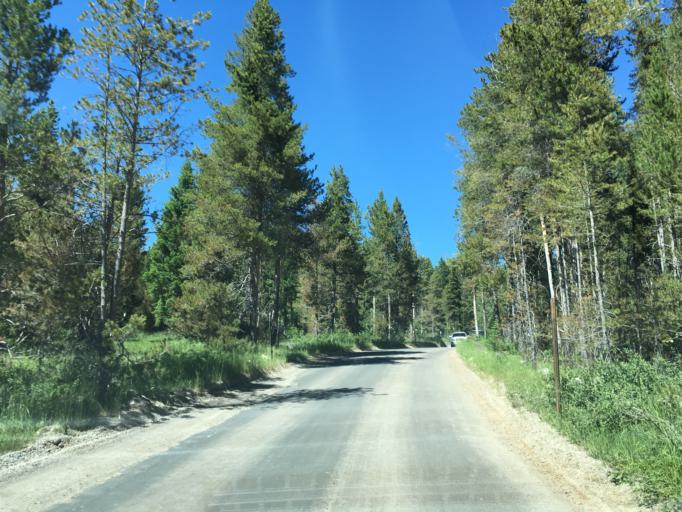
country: US
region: Wyoming
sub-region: Teton County
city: Moose Wilson Road
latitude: 43.6214
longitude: -110.7877
